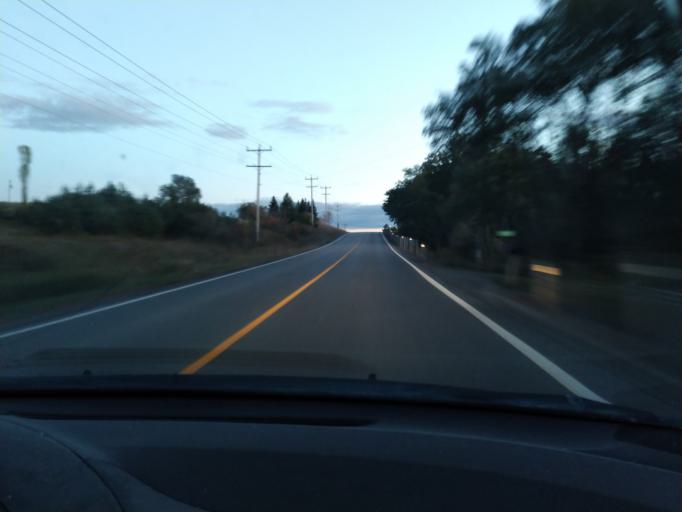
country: CA
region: Ontario
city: Innisfil
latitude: 44.2197
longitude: -79.6703
